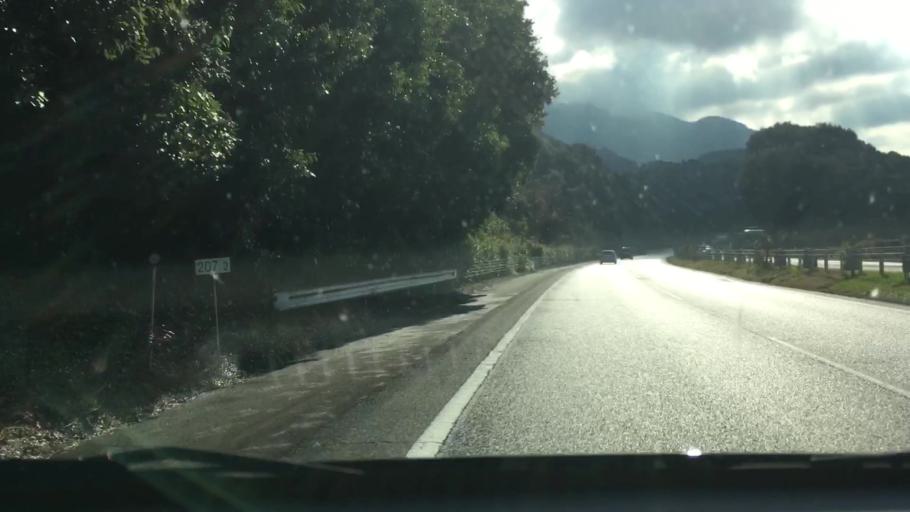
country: JP
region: Kumamoto
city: Matsubase
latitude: 32.5531
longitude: 130.6943
